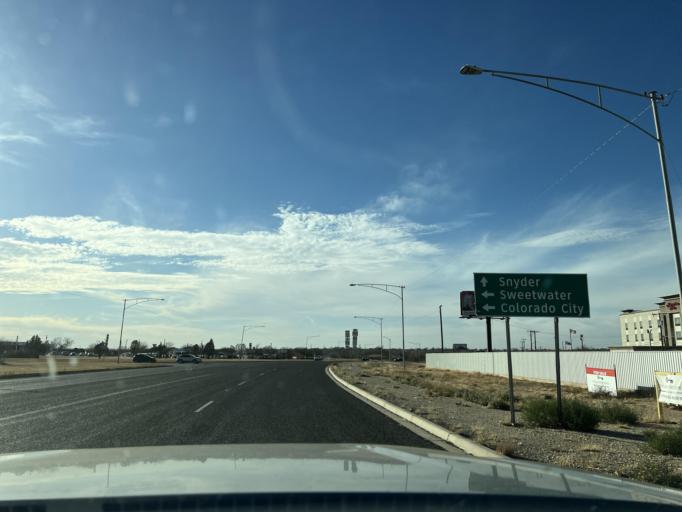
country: US
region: Texas
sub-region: Scurry County
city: Snyder
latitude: 32.7024
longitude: -100.8774
